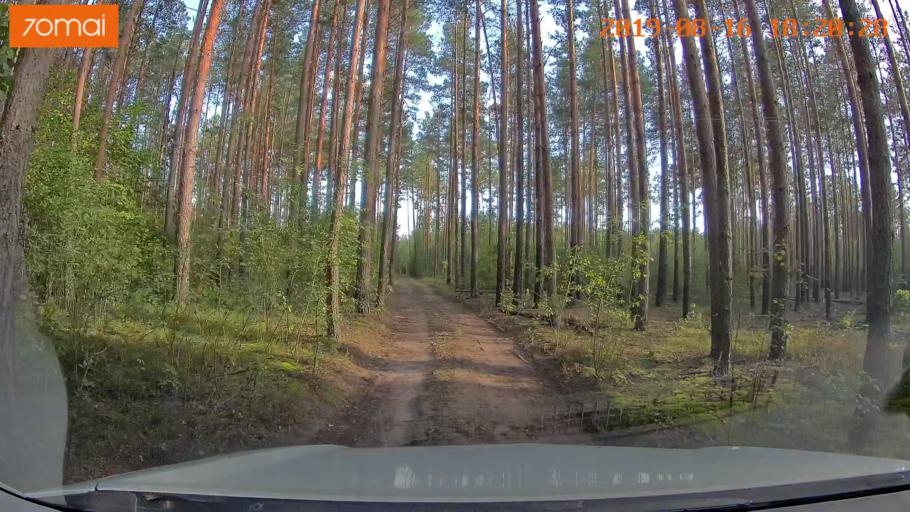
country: BY
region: Mogilev
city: Asipovichy
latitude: 53.2076
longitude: 28.6333
